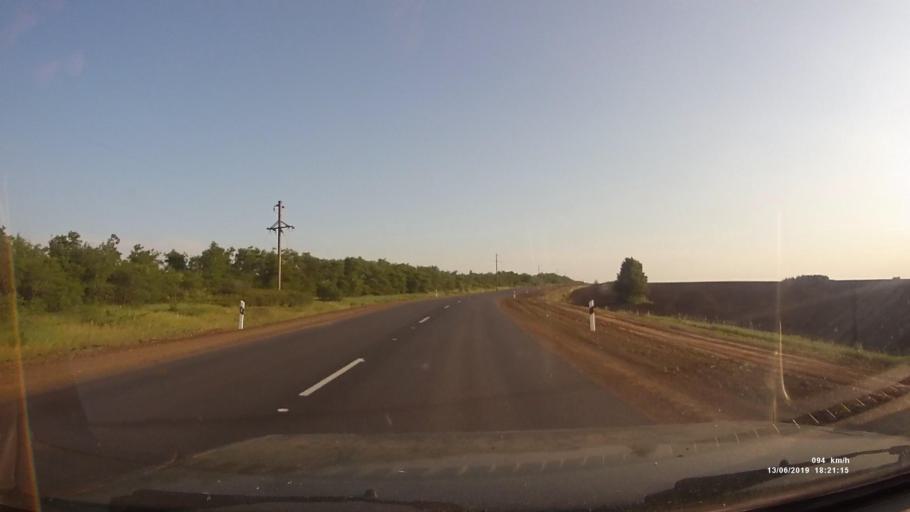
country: RU
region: Rostov
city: Kazanskaya
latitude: 49.8728
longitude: 41.2933
